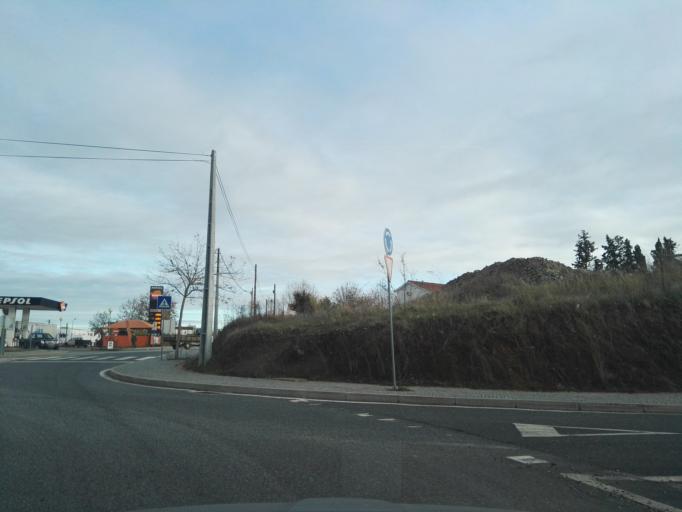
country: PT
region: Evora
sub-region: Redondo
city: Redondo
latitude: 38.6516
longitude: -7.5508
